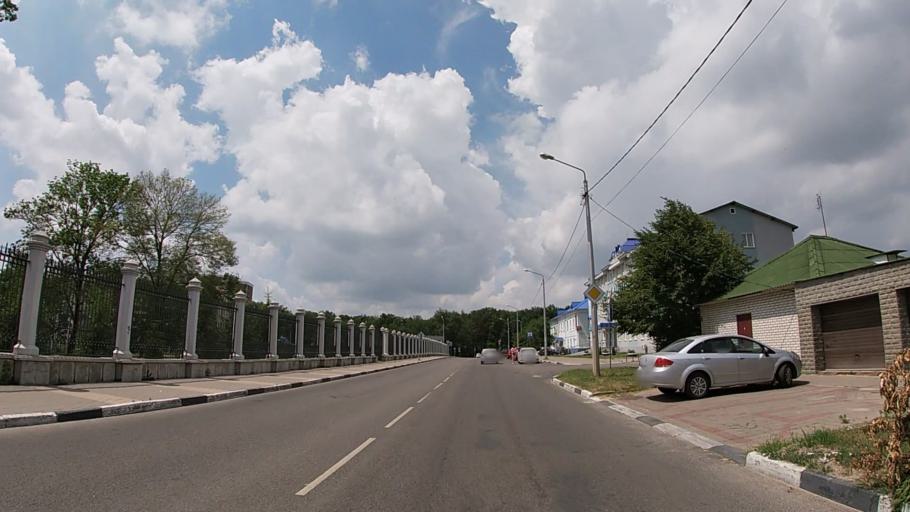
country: RU
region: Belgorod
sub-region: Belgorodskiy Rayon
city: Belgorod
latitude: 50.6066
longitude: 36.5935
